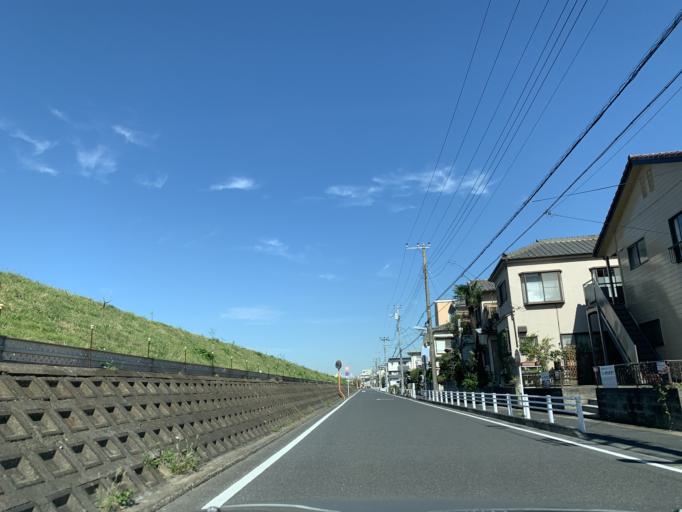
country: JP
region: Tokyo
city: Urayasu
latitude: 35.6508
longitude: 139.8869
